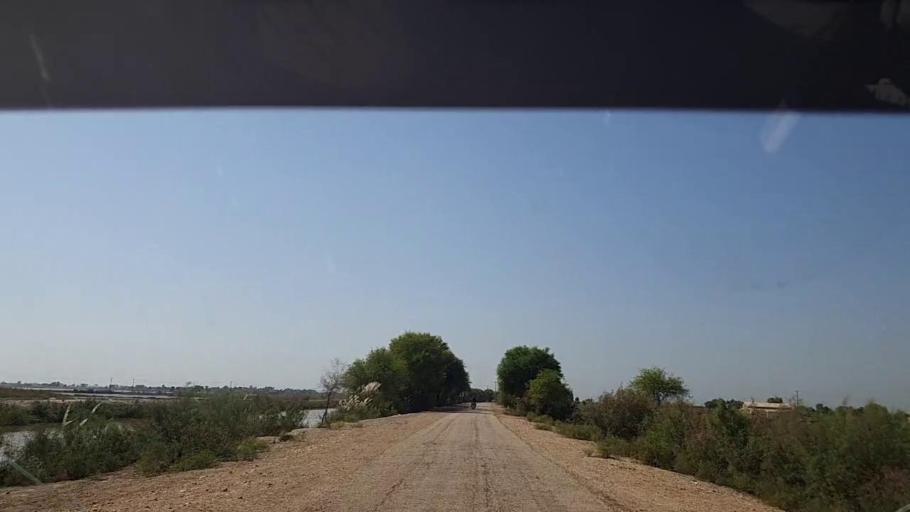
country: PK
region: Sindh
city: Ghauspur
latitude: 28.1959
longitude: 69.0480
